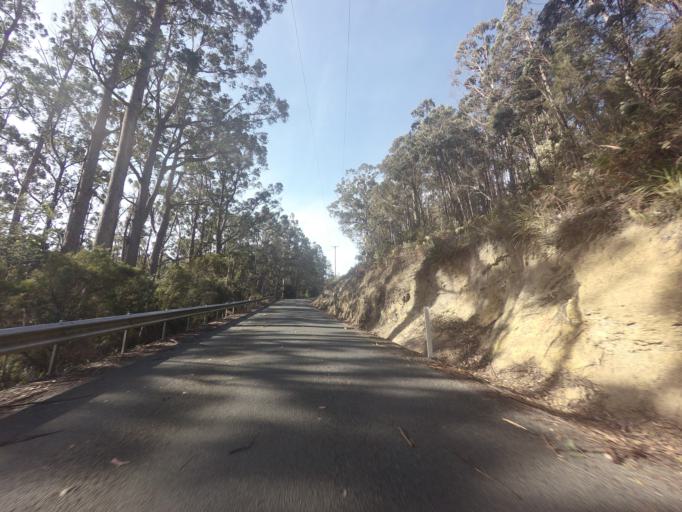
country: AU
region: Tasmania
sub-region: Kingborough
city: Kettering
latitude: -43.1681
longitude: 147.1853
